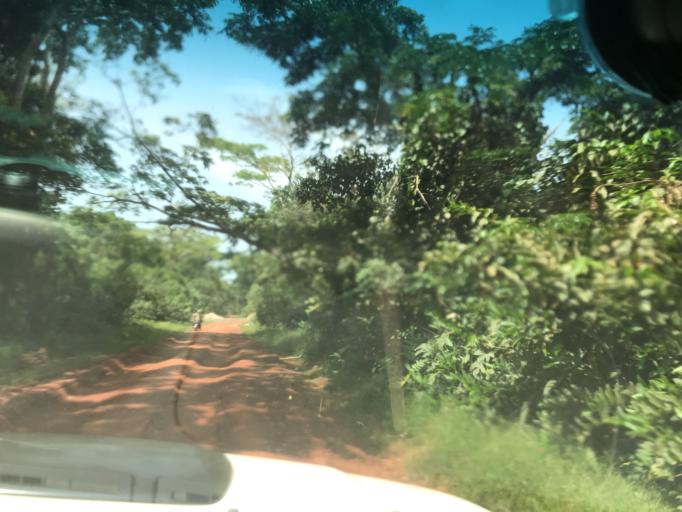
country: CD
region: Eastern Province
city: Aketi
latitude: 2.8822
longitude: 23.9705
